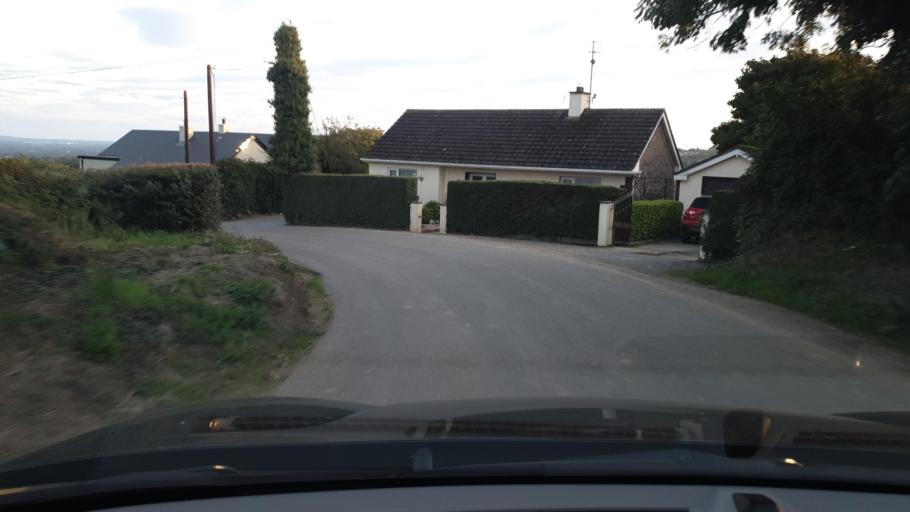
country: IE
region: Leinster
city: Balrothery
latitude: 53.5692
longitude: -6.2415
